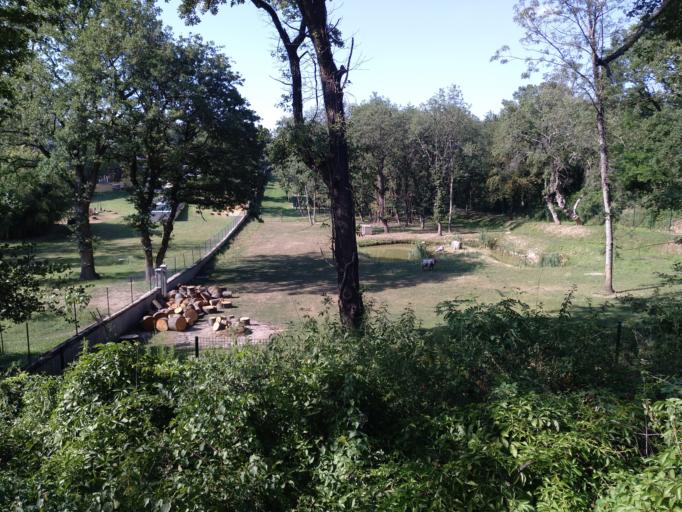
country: FR
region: Rhone-Alpes
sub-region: Departement de l'Isere
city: Chasse-sur-Rhone
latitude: 45.5950
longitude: 4.8050
